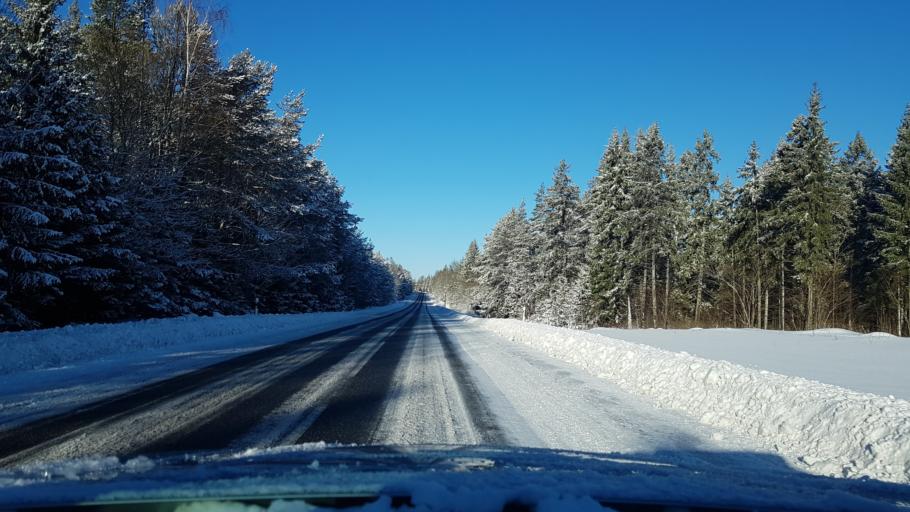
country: EE
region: Hiiumaa
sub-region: Kaerdla linn
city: Kardla
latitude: 58.9711
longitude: 22.8257
